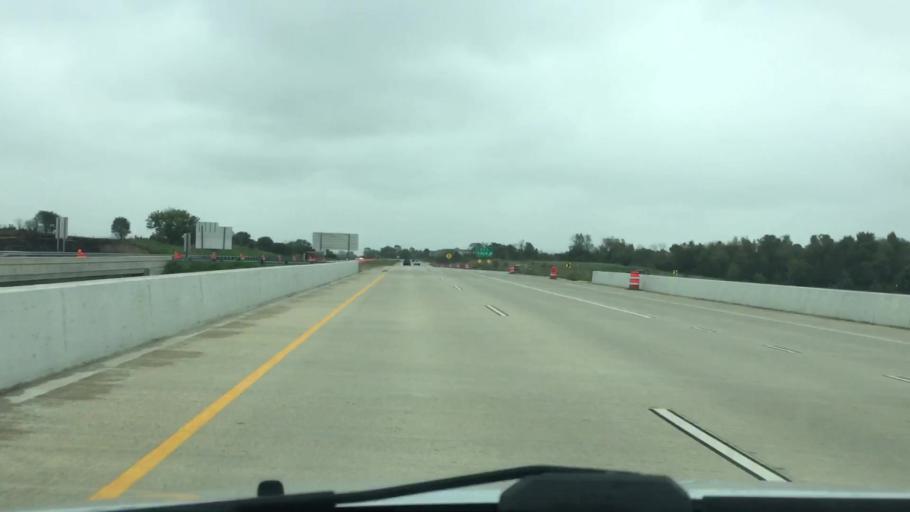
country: US
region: Wisconsin
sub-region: Walworth County
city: Lake Geneva
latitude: 42.5942
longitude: -88.4090
